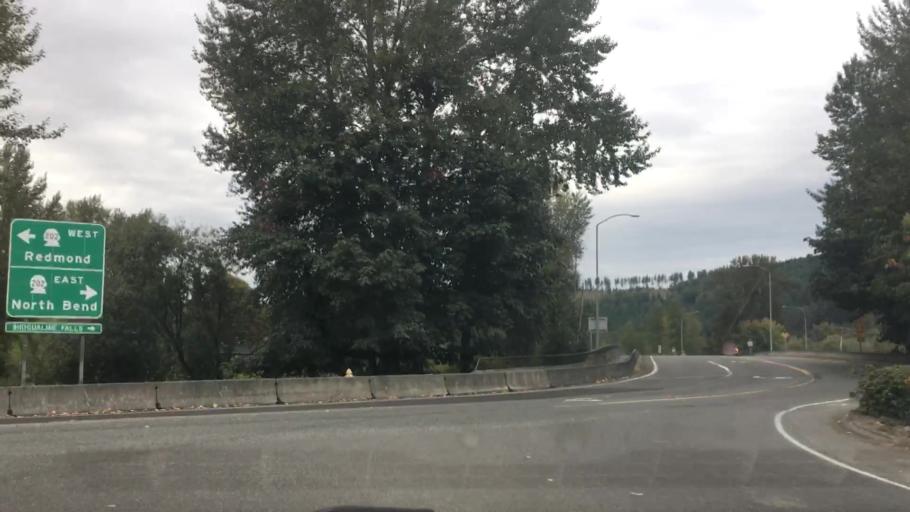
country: US
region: Washington
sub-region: King County
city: Fall City
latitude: 47.5641
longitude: -121.8895
